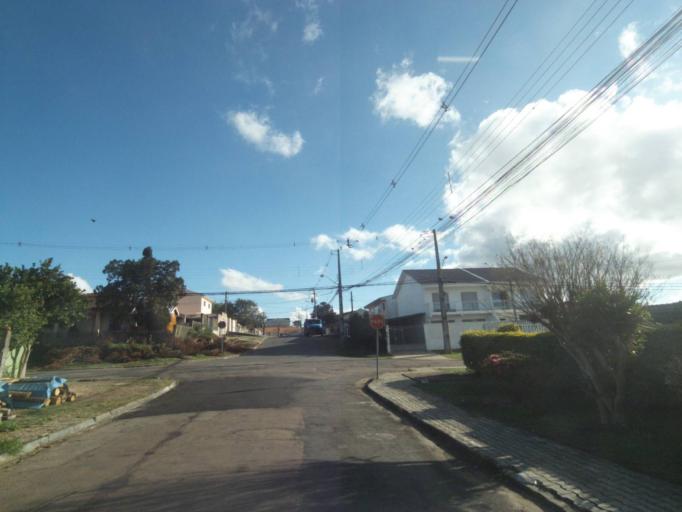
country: BR
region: Parana
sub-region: Sao Jose Dos Pinhais
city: Sao Jose dos Pinhais
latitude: -25.5263
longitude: -49.2850
